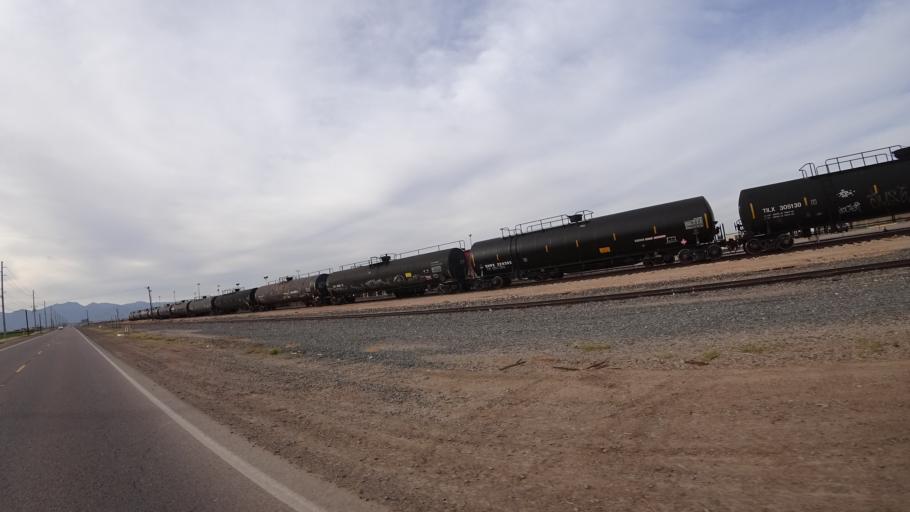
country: US
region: Arizona
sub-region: Maricopa County
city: Citrus Park
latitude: 33.5659
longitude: -112.3773
